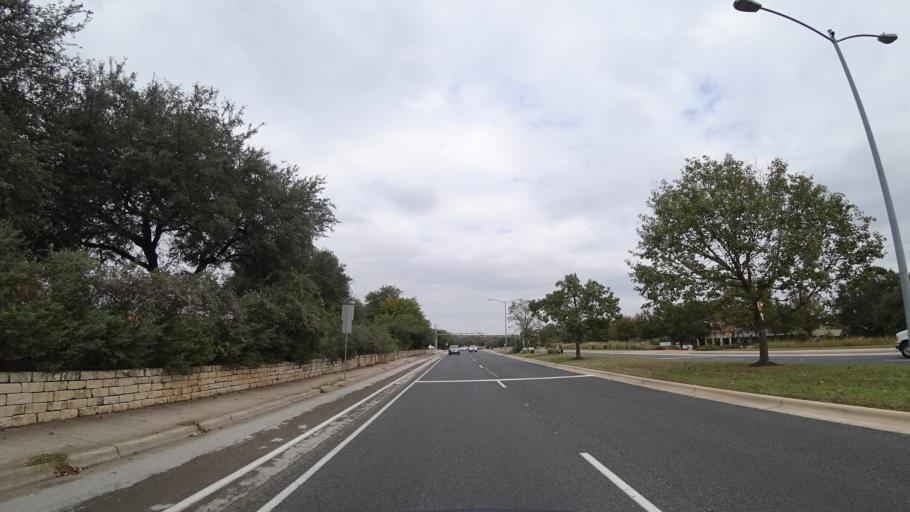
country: US
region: Texas
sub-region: Travis County
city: Shady Hollow
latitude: 30.2105
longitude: -97.8768
